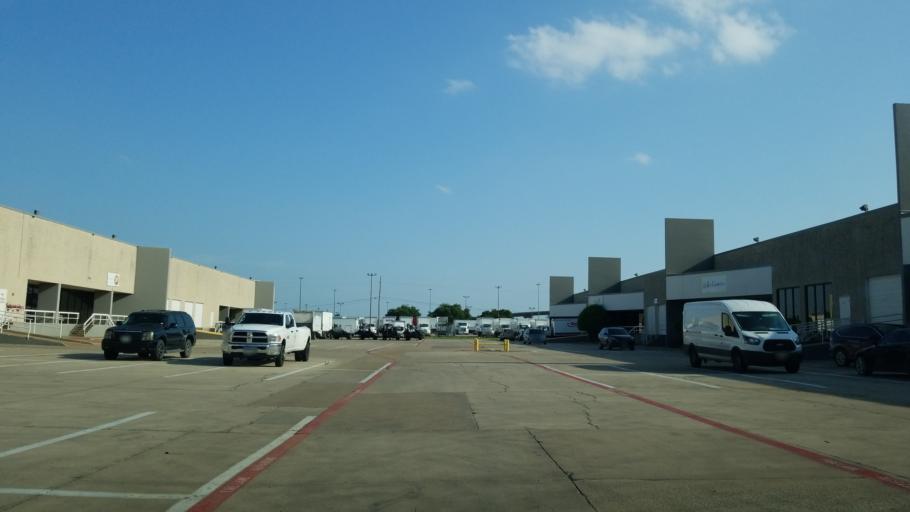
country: US
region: Texas
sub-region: Dallas County
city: Farmers Branch
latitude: 32.8733
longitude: -96.8958
